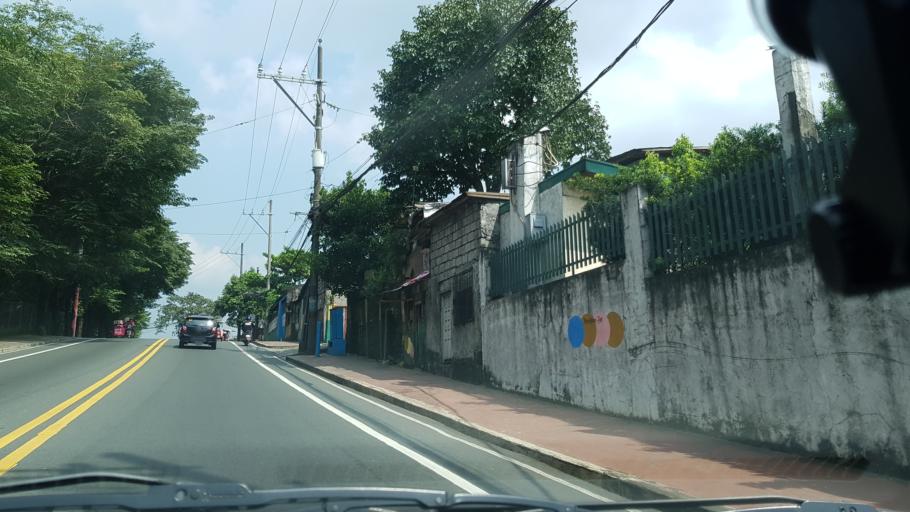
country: PH
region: Calabarzon
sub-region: Province of Rizal
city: San Mateo
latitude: 14.6626
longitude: 121.1218
